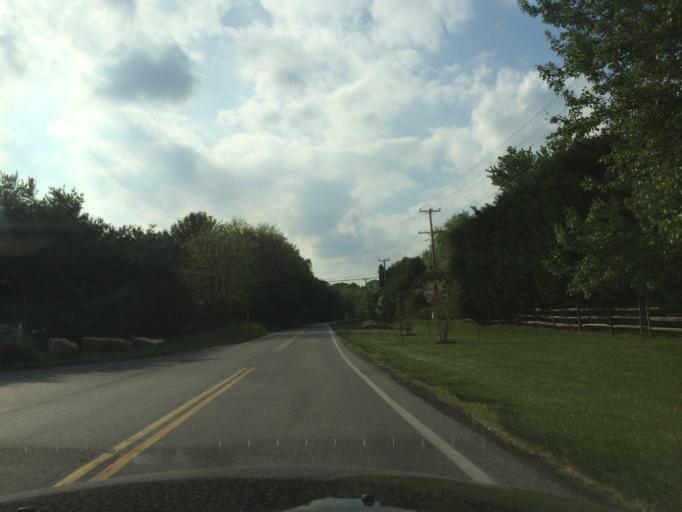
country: US
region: Maryland
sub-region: Howard County
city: Highland
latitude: 39.1860
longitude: -76.9692
